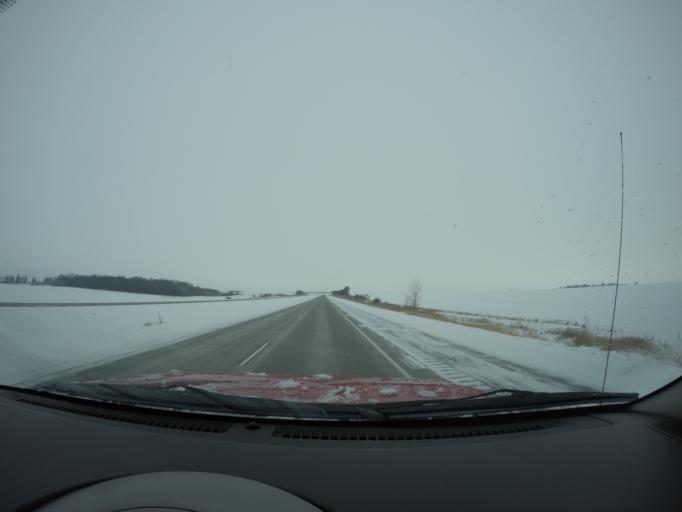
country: US
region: Minnesota
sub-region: Olmsted County
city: Eyota
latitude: 43.9552
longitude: -92.1690
